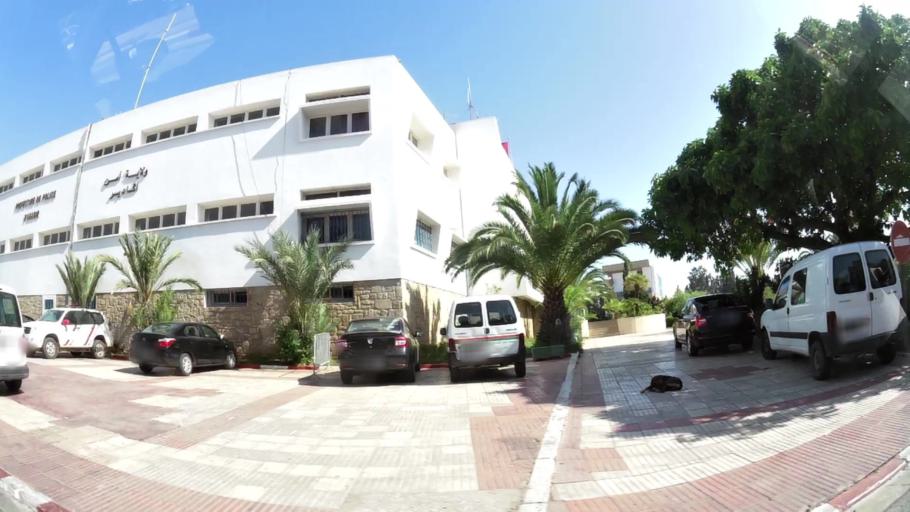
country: MA
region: Souss-Massa-Draa
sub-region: Agadir-Ida-ou-Tnan
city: Agadir
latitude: 30.4183
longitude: -9.5916
